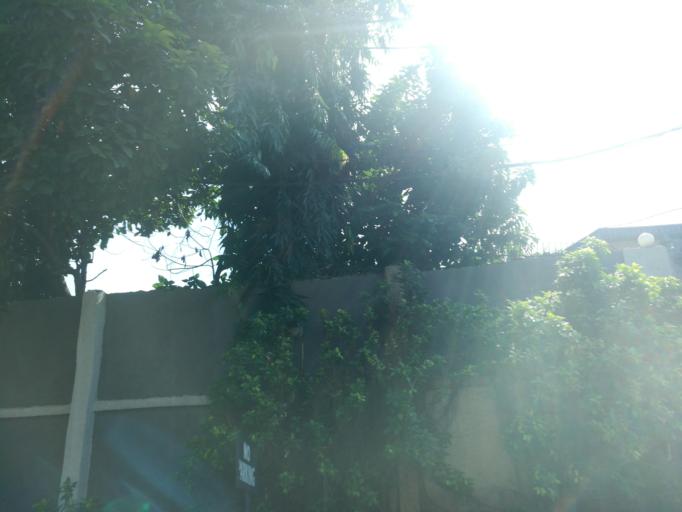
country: NG
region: Lagos
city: Ikeja
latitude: 6.6033
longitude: 3.3423
